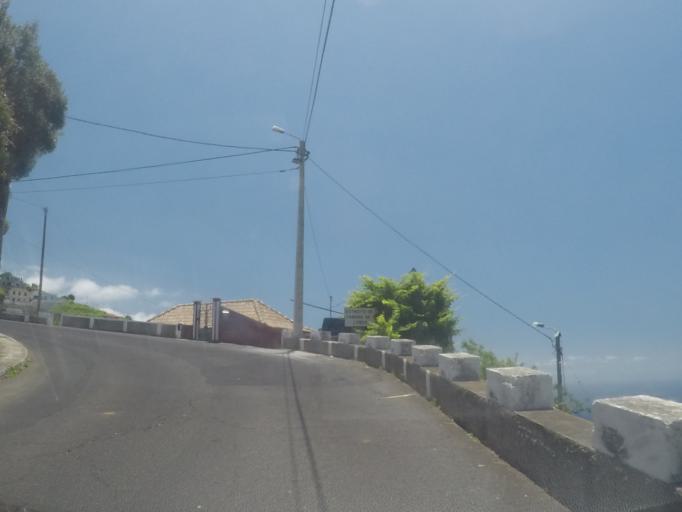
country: PT
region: Madeira
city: Camara de Lobos
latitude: 32.6703
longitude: -16.9839
